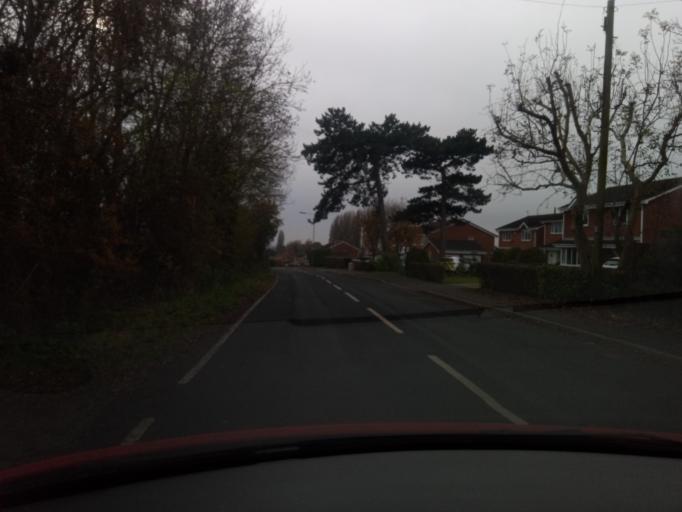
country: GB
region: England
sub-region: Derbyshire
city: Little Eaton
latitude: 52.9407
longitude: -1.4213
